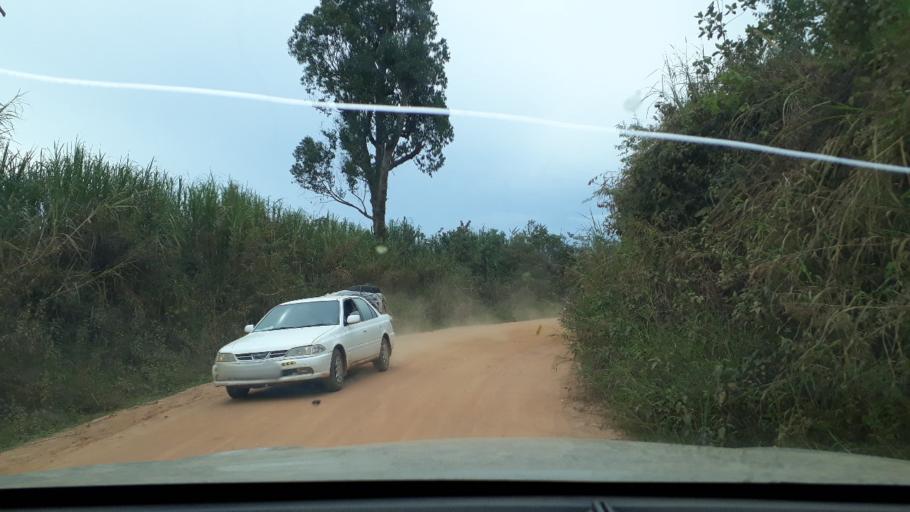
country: CD
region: Eastern Province
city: Bunia
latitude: 1.8480
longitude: 30.4727
